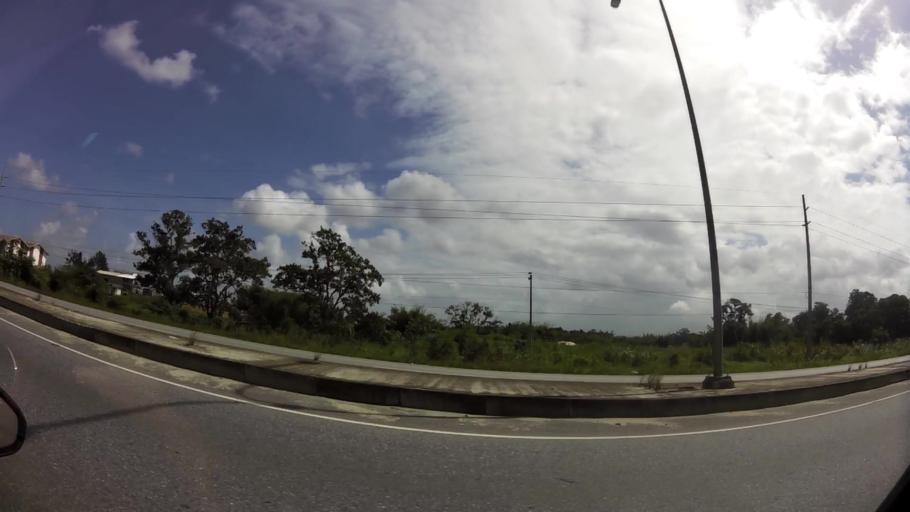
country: TT
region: Borough of Arima
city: Arima
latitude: 10.6117
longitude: -61.2645
